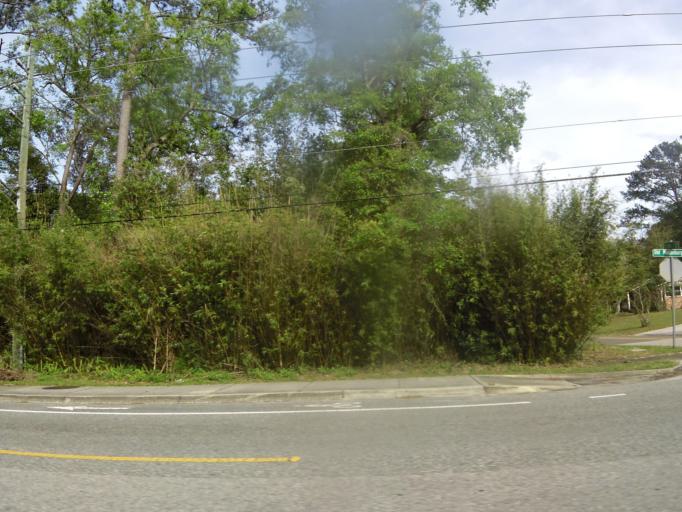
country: US
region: Florida
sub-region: Clay County
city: Bellair-Meadowbrook Terrace
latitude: 30.2834
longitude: -81.7681
